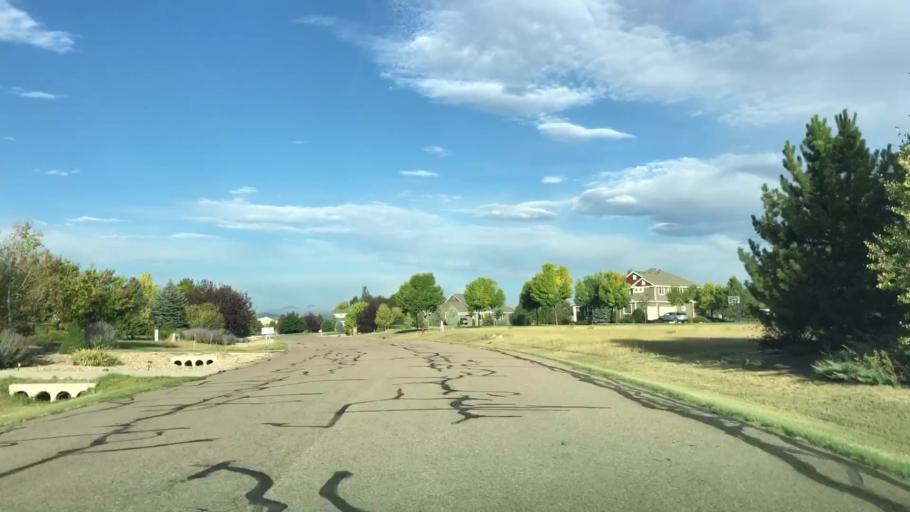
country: US
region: Colorado
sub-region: Weld County
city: Windsor
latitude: 40.4376
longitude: -104.9554
